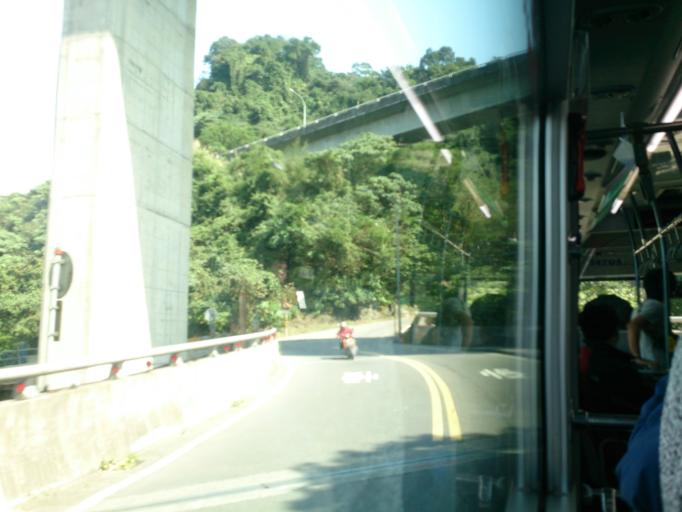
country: TW
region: Taipei
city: Taipei
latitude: 24.9963
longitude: 121.5937
